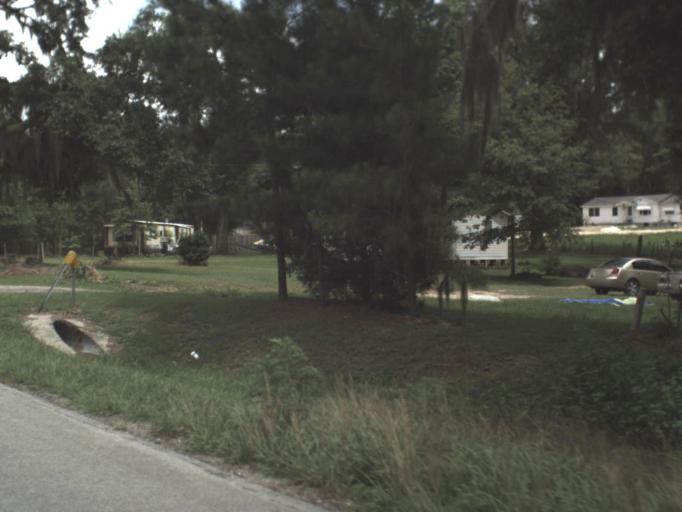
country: US
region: Florida
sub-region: Madison County
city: Madison
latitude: 30.4716
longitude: -83.3635
